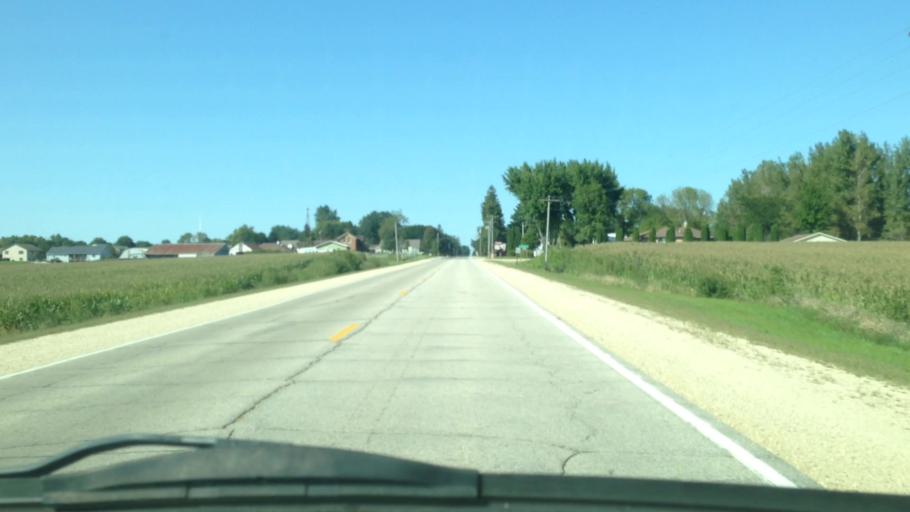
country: US
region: Minnesota
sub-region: Winona County
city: Lewiston
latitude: 43.9735
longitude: -91.8692
